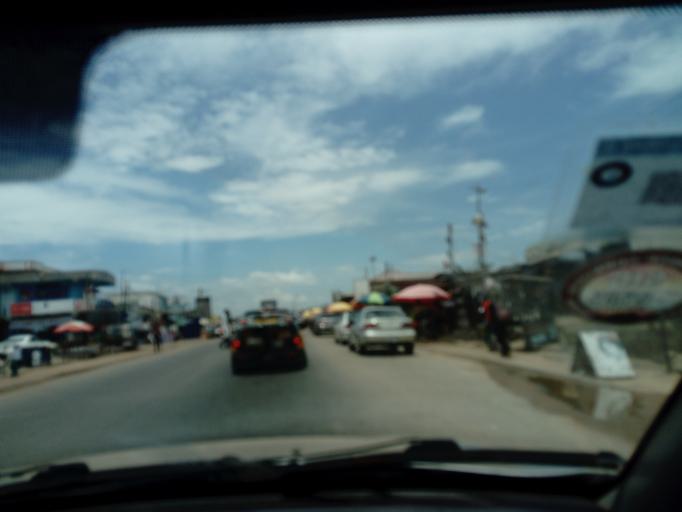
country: GH
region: Central
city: Cape Coast
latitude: 5.1313
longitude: -1.2754
